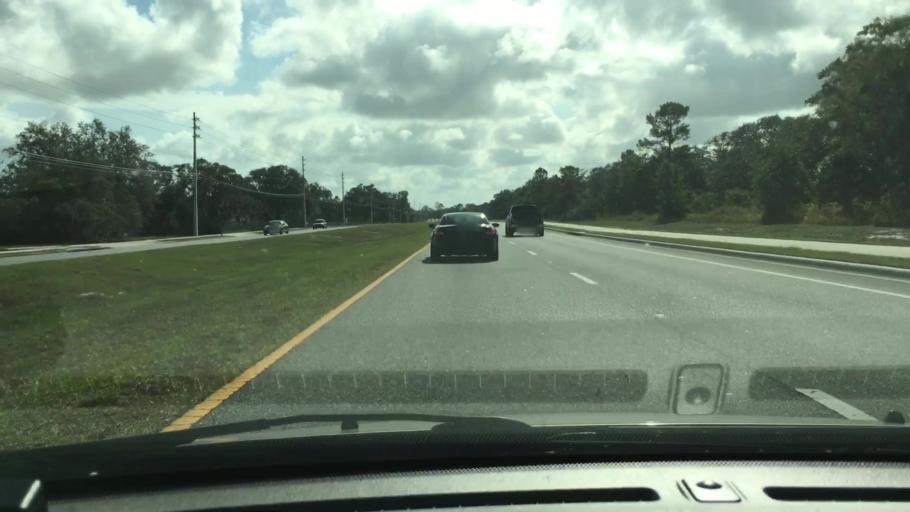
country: US
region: Florida
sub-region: Osceola County
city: Saint Cloud
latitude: 28.2881
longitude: -81.2396
